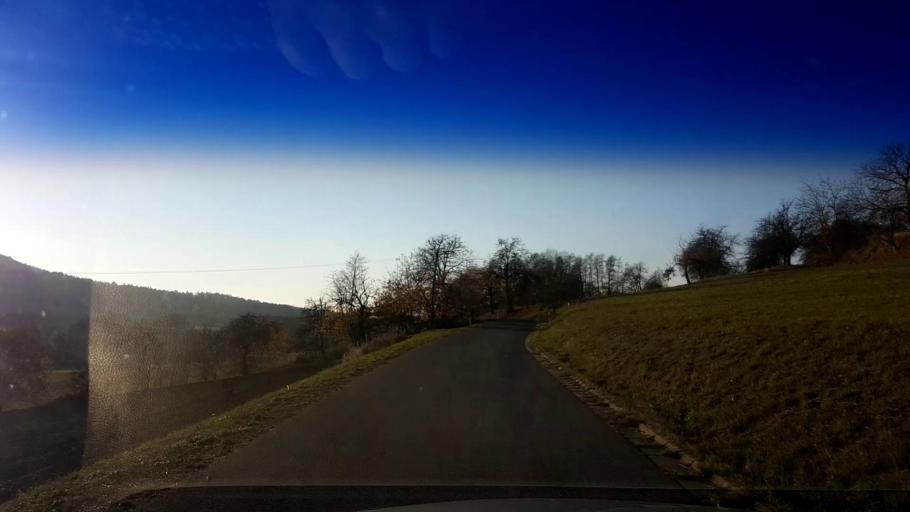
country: DE
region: Bavaria
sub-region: Upper Franconia
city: Schesslitz
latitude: 49.9486
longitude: 11.0520
